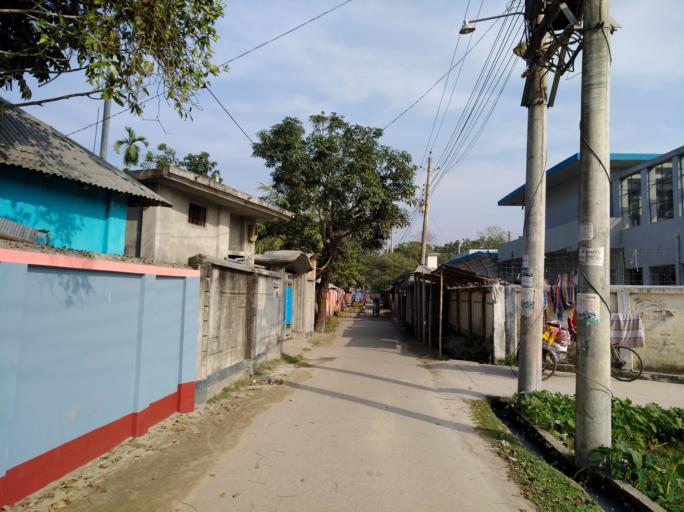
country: BD
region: Rajshahi
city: Saidpur
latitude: 25.9337
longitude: 88.8424
